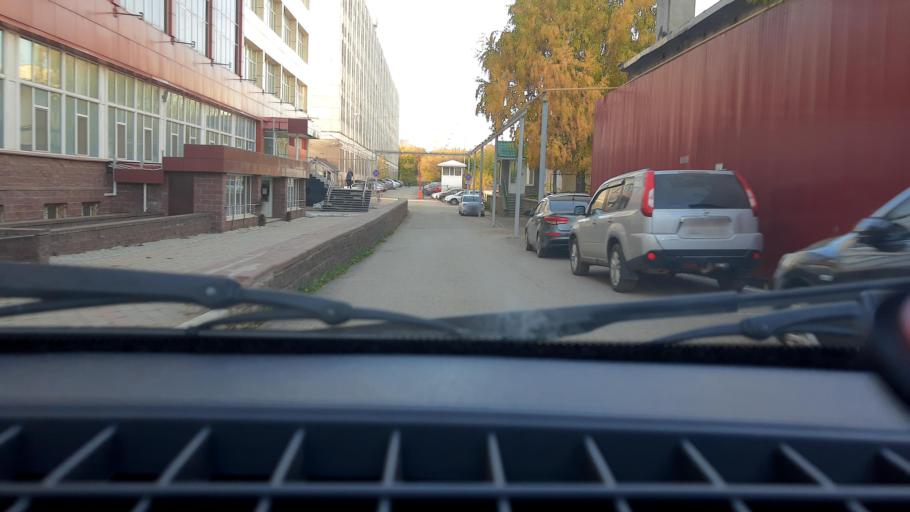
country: RU
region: Bashkortostan
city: Ufa
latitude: 54.7507
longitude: 56.0082
